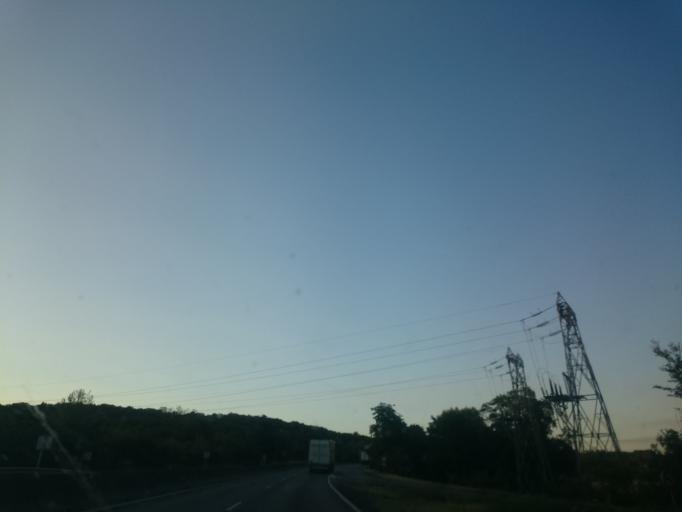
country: FR
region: Ile-de-France
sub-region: Departement de l'Essonne
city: Etrechy
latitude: 48.5043
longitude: 2.2005
